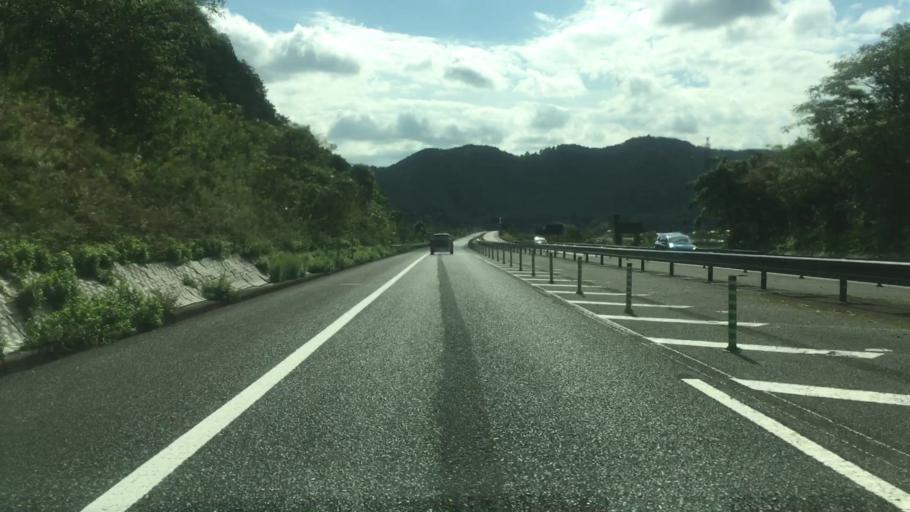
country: JP
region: Kyoto
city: Fukuchiyama
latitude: 35.2370
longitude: 135.0173
